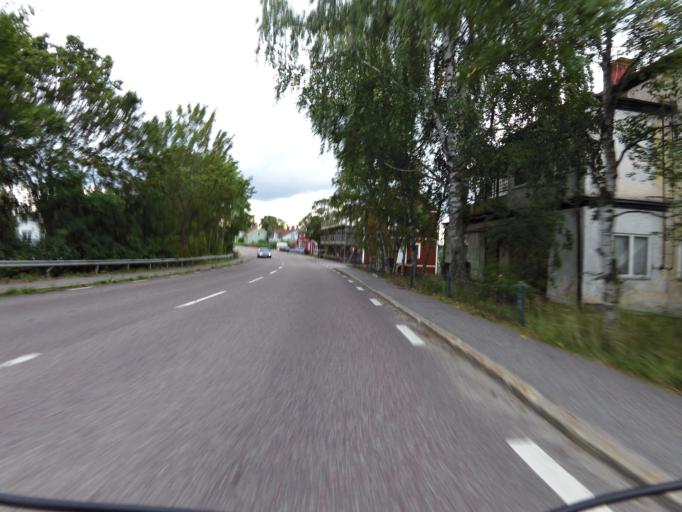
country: SE
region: Gaevleborg
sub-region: Ockelbo Kommun
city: Ockelbo
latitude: 60.8998
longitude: 16.7211
